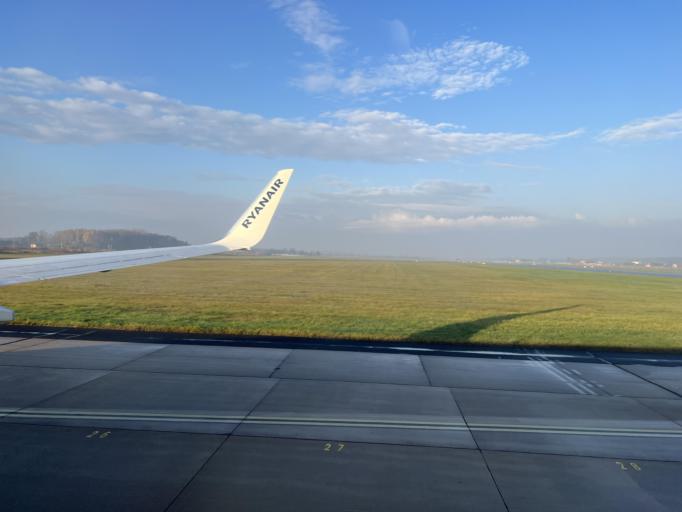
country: PL
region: Silesian Voivodeship
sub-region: Powiat tarnogorski
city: Ozarowice
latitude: 50.4734
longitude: 19.0662
